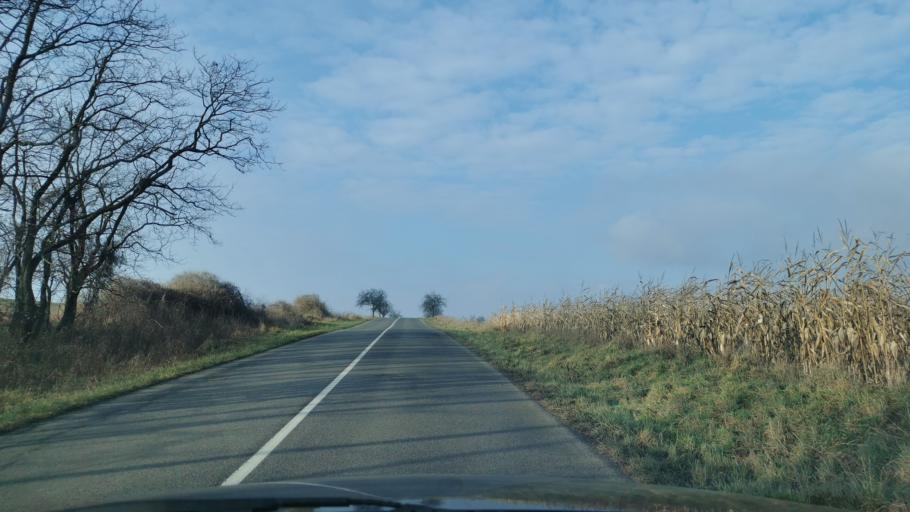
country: SK
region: Trnavsky
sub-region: Okres Senica
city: Senica
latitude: 48.7126
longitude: 17.3326
